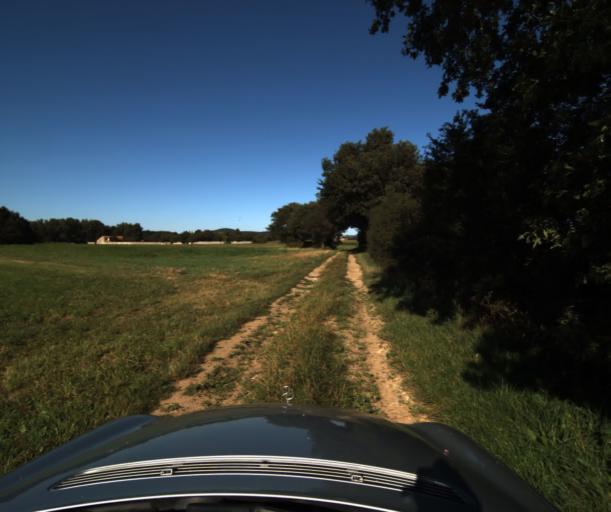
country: FR
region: Midi-Pyrenees
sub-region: Departement de l'Ariege
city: Lavelanet
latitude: 42.9858
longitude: 1.8972
